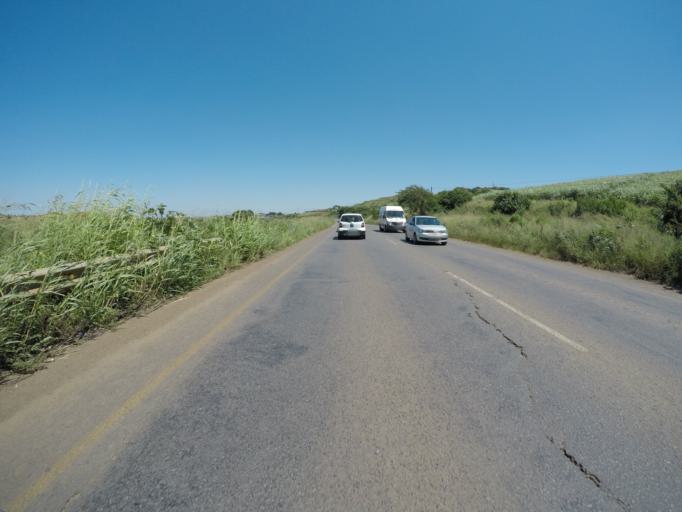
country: ZA
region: KwaZulu-Natal
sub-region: uThungulu District Municipality
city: Empangeni
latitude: -28.7514
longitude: 31.8776
